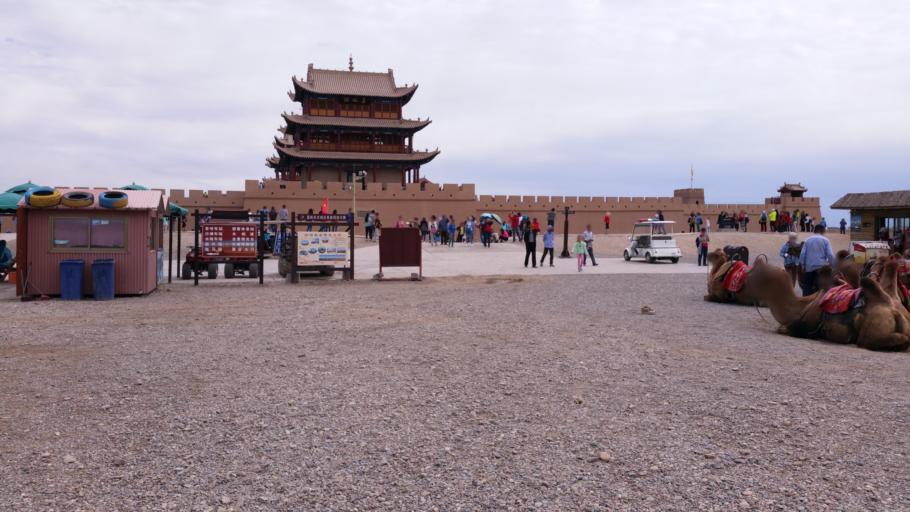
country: CN
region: Gansu Sheng
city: Jiayuguan
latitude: 39.8010
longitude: 98.2138
